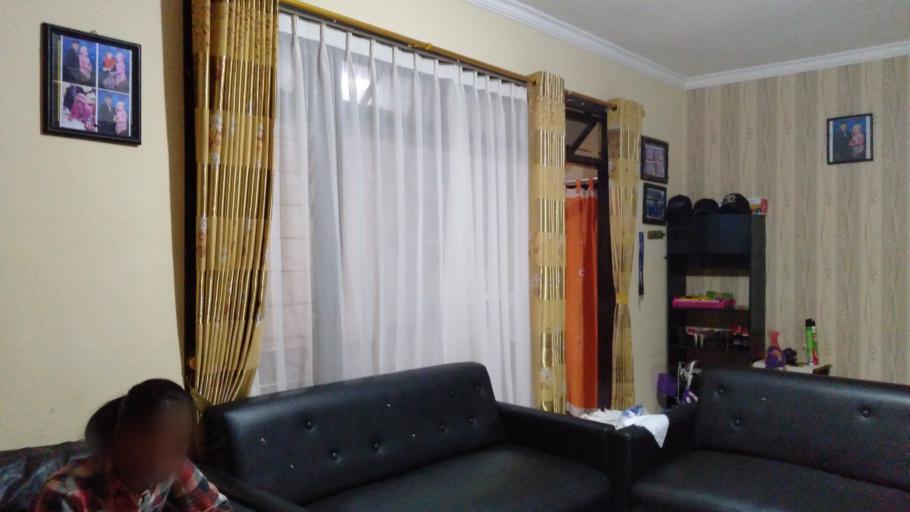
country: ID
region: East Java
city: Batu
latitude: -7.8674
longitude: 112.5179
